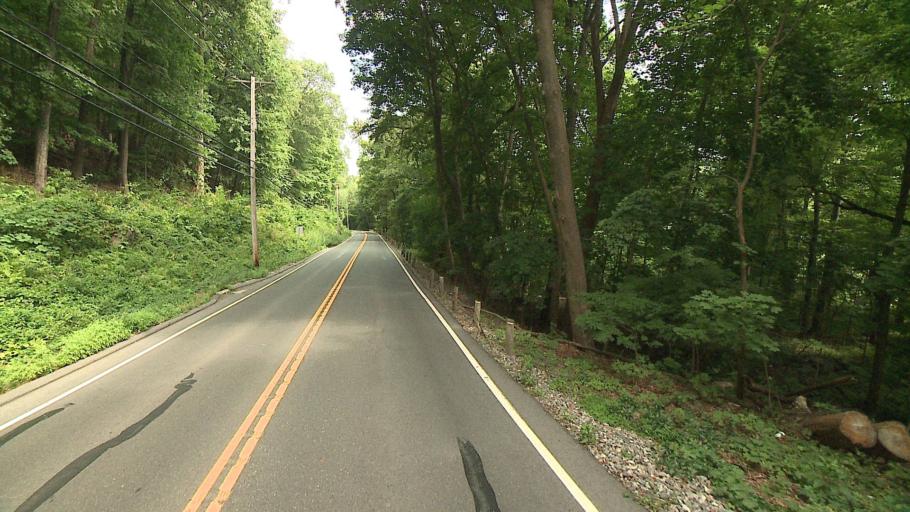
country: US
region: New York
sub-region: Putnam County
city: Putnam Lake
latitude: 41.4854
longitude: -73.4644
